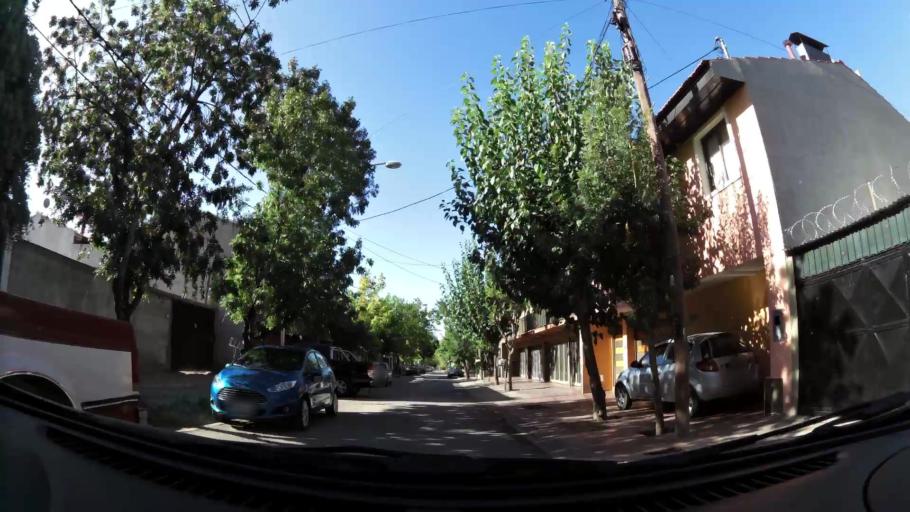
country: AR
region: Mendoza
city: Mendoza
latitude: -32.9063
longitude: -68.8159
